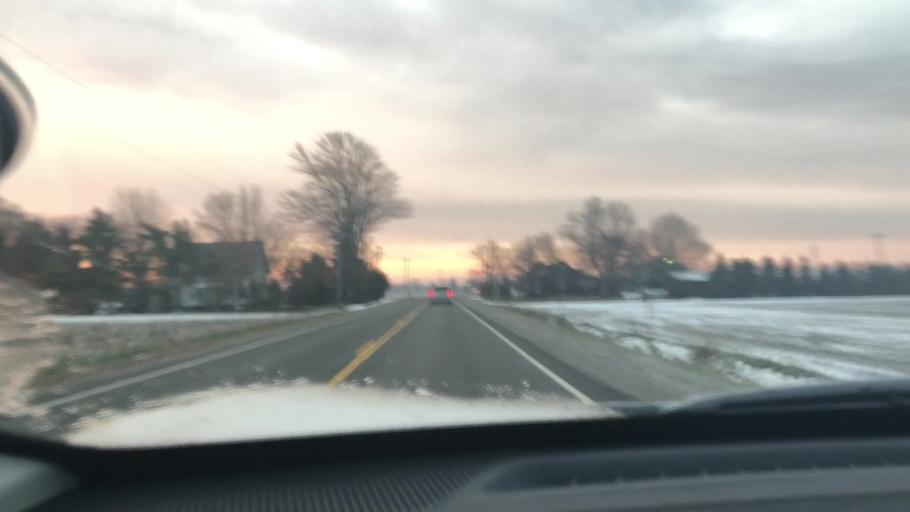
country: US
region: Michigan
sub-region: Saginaw County
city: Zilwaukee
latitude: 43.5092
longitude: -83.8361
